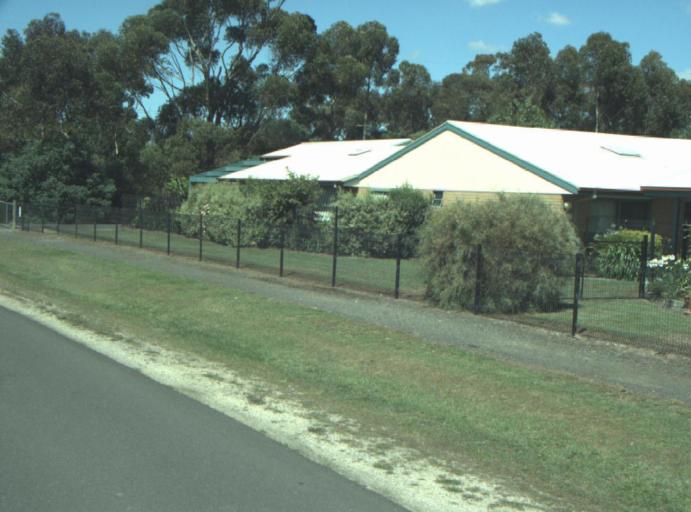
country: AU
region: Victoria
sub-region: Greater Geelong
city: Breakwater
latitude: -38.1992
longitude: 144.3624
